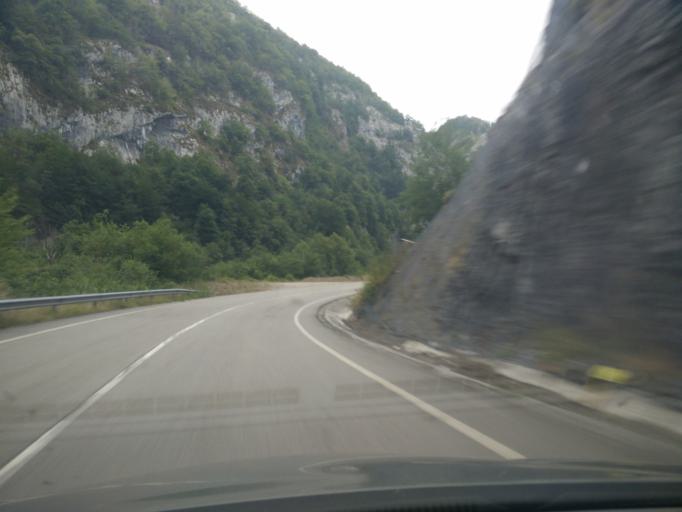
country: ES
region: Asturias
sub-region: Province of Asturias
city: Campo de Caso
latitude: 43.1817
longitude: -5.3643
